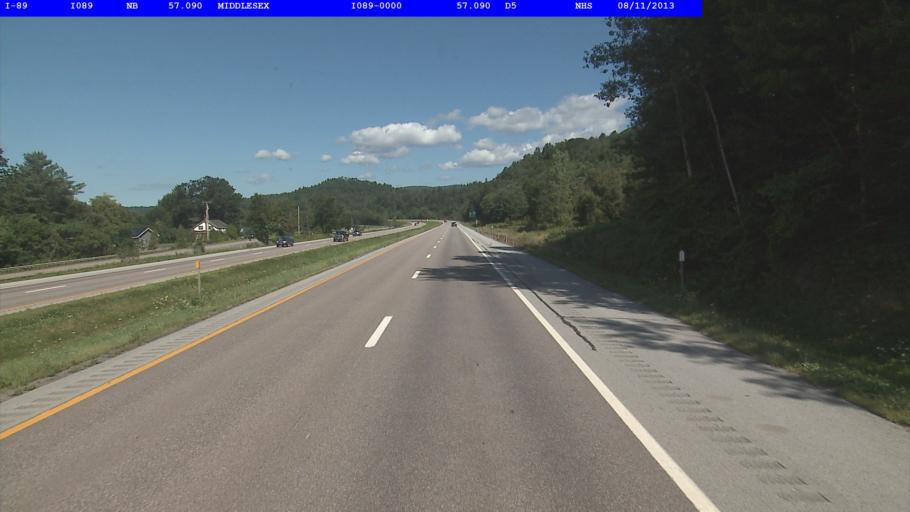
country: US
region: Vermont
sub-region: Washington County
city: Montpelier
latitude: 44.2836
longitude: -72.6610
